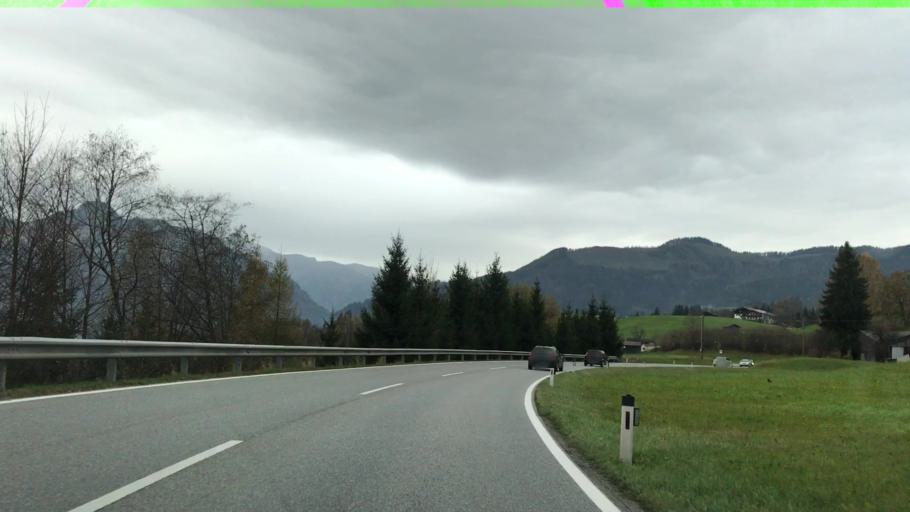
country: AT
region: Tyrol
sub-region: Politischer Bezirk Kitzbuhel
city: Kossen
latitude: 47.6524
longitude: 12.4311
